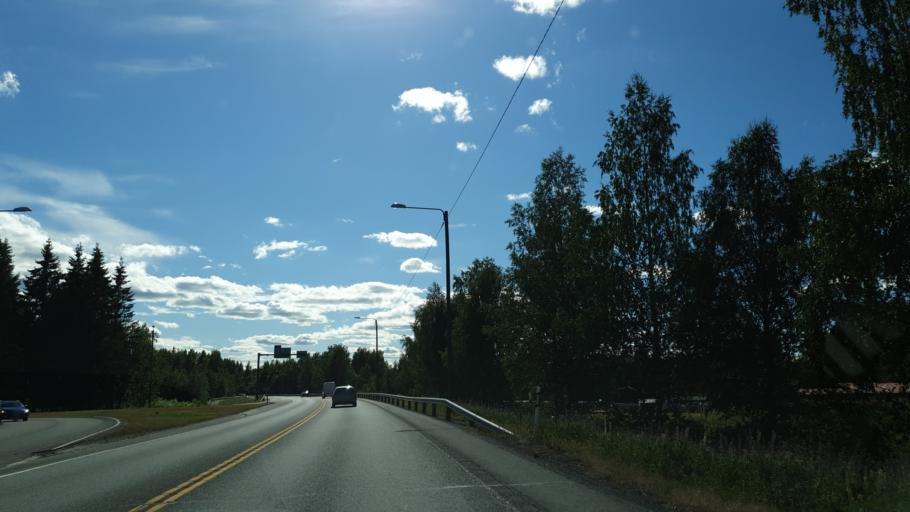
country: FI
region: Southern Savonia
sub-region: Mikkeli
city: Mikkeli
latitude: 61.6428
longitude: 27.0824
